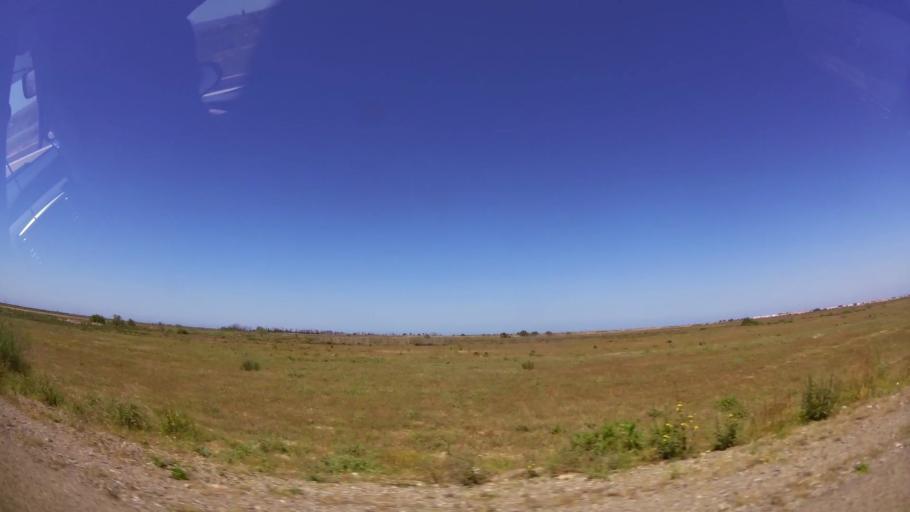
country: MA
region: Oriental
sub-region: Berkane-Taourirt
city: Madagh
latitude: 35.1045
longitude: -2.3434
